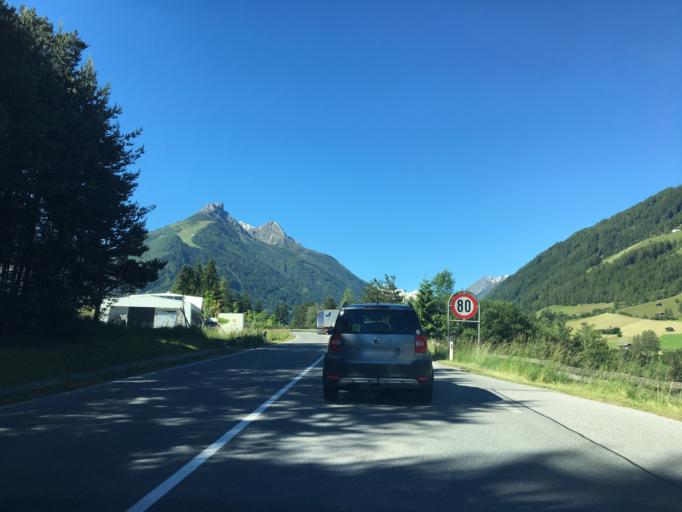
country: AT
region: Tyrol
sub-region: Politischer Bezirk Innsbruck Land
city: Fulpmes
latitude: 47.1383
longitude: 11.3418
